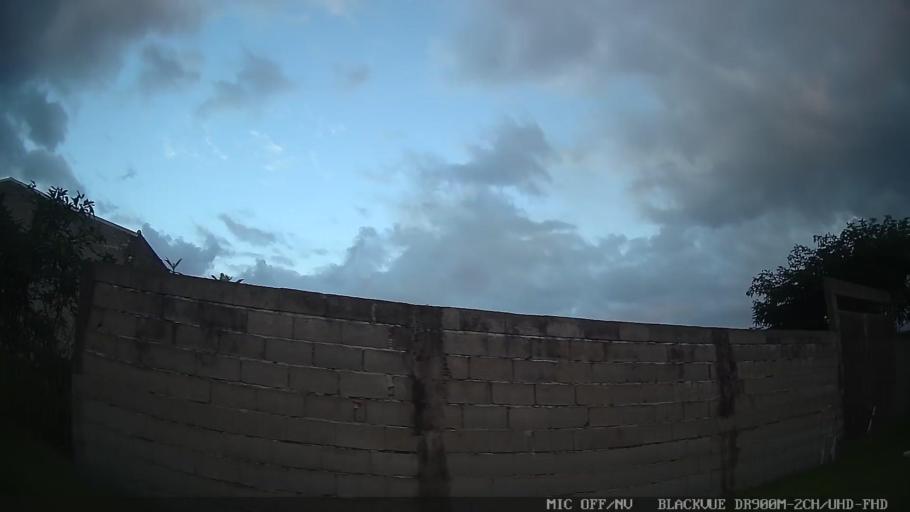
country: BR
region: Sao Paulo
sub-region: Itanhaem
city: Itanhaem
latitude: -24.1828
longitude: -46.8347
